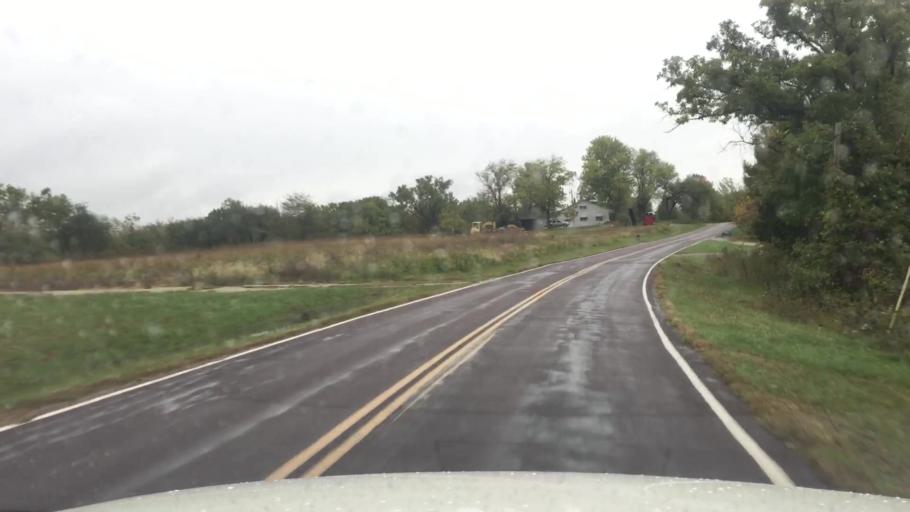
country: US
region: Missouri
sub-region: Boone County
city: Ashland
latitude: 38.7144
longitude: -92.2831
